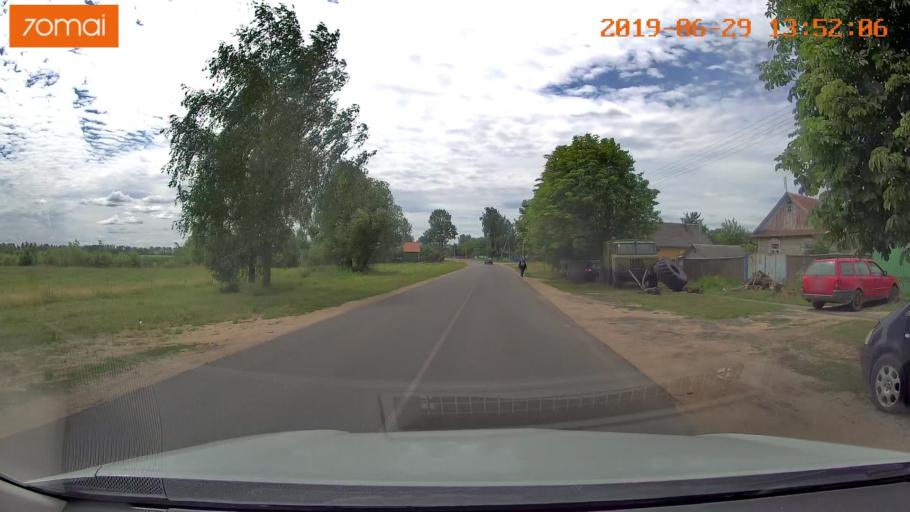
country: BY
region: Minsk
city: Slutsk
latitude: 52.9974
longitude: 27.5587
